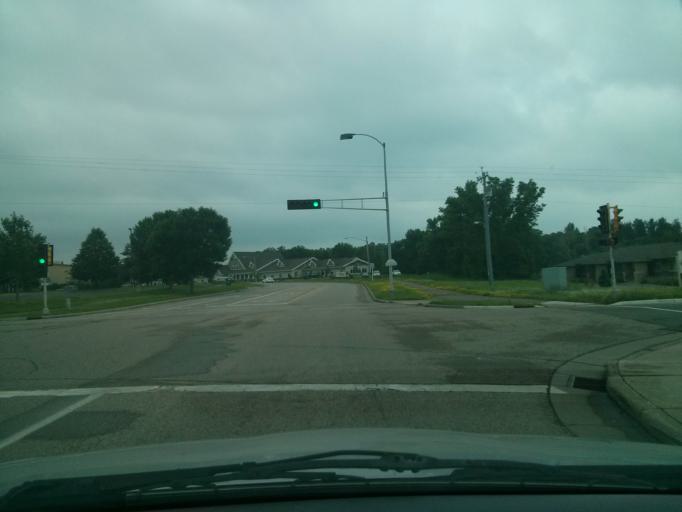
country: US
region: Wisconsin
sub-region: Saint Croix County
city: Hudson
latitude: 44.9621
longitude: -92.7437
